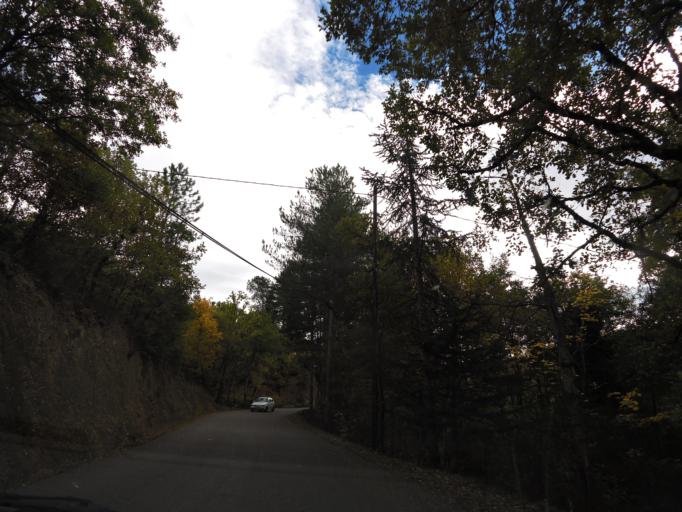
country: FR
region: Languedoc-Roussillon
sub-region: Departement du Gard
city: Lasalle
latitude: 44.0319
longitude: 3.8726
